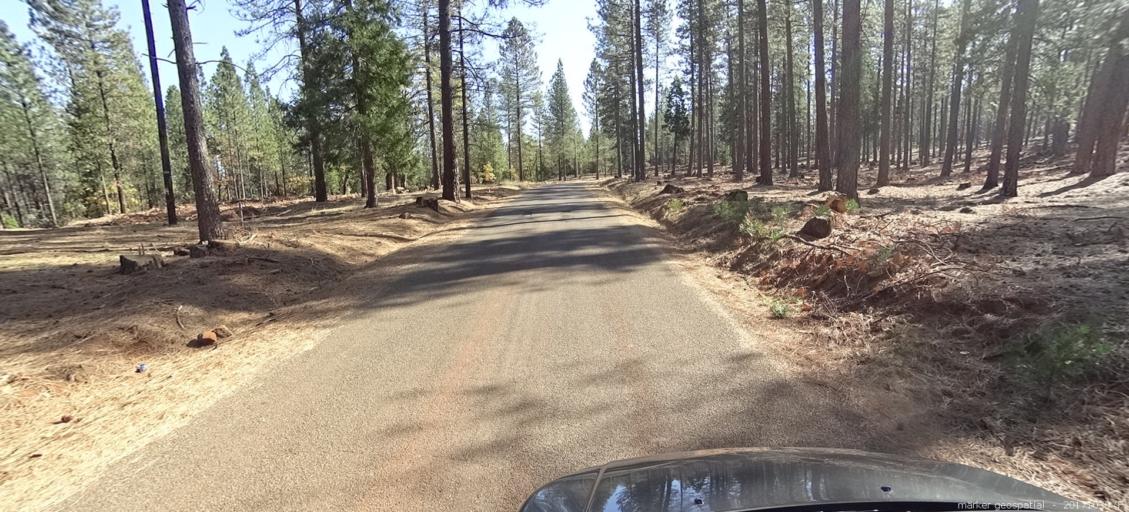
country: US
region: California
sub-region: Shasta County
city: Shingletown
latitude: 40.6217
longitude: -121.8938
